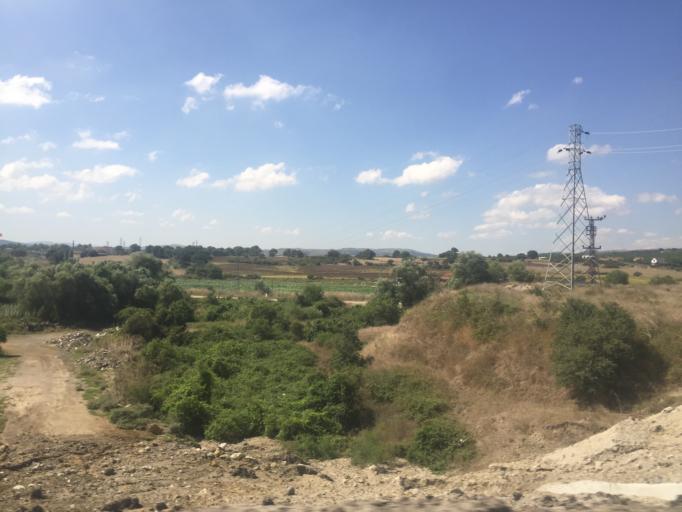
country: TR
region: Balikesir
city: Susurluk
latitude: 39.9581
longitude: 28.1679
